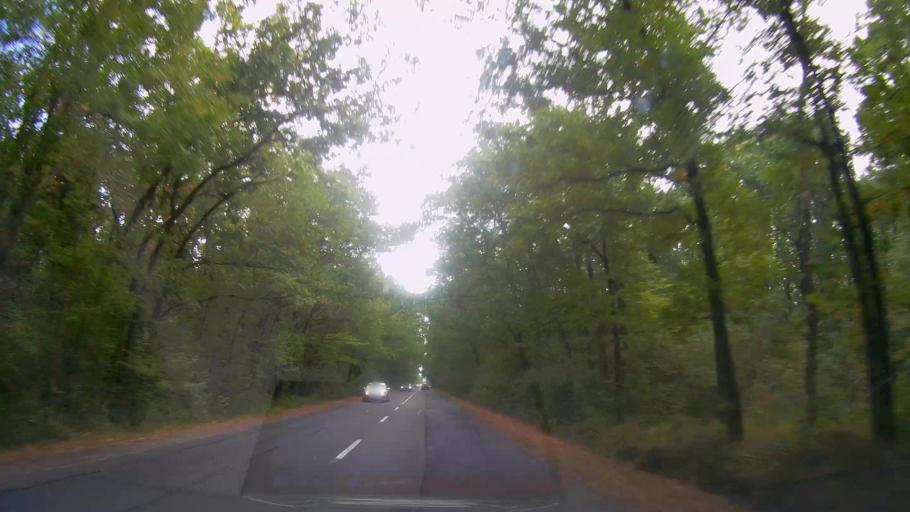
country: BG
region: Burgas
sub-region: Obshtina Primorsko
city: Primorsko
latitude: 42.2801
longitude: 27.7386
